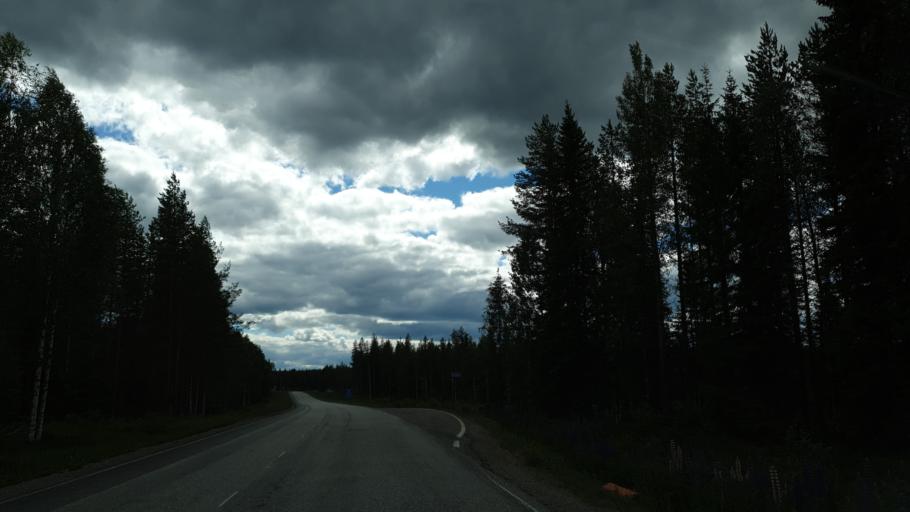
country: FI
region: Kainuu
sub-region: Kehys-Kainuu
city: Kuhmo
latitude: 63.9783
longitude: 29.6419
